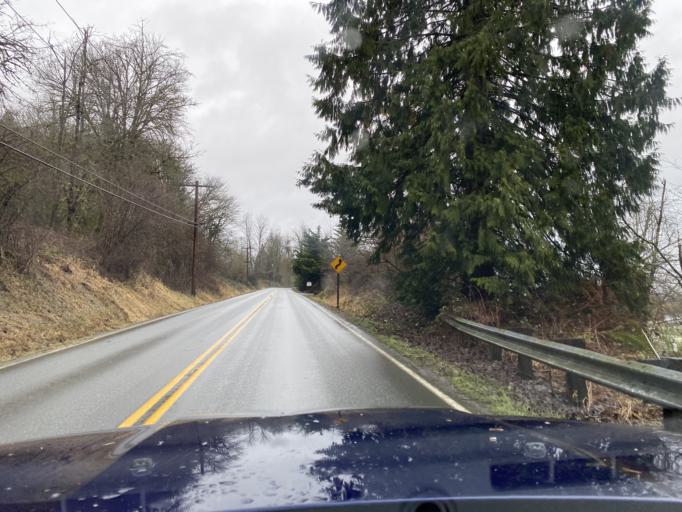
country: US
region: Washington
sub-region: King County
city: Duvall
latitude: 47.7257
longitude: -122.0101
